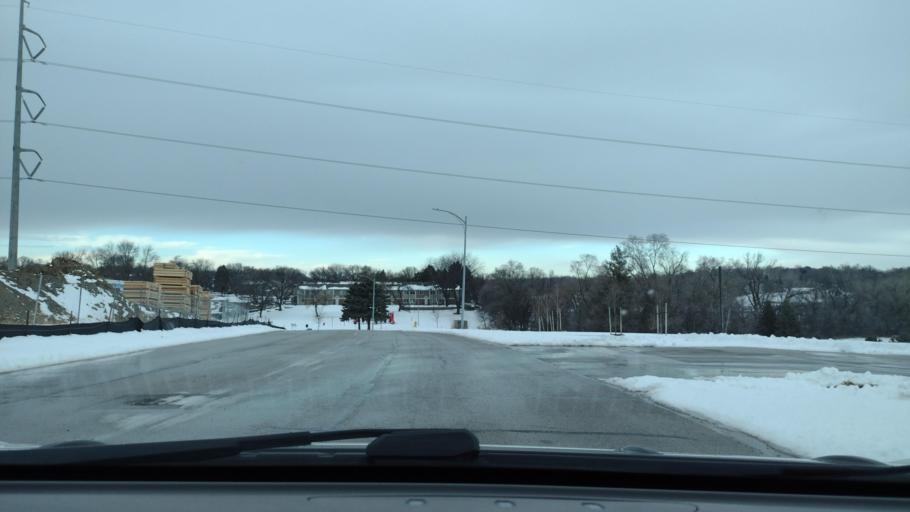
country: US
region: Nebraska
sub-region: Sarpy County
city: Bellevue
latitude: 41.1780
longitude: -95.9318
